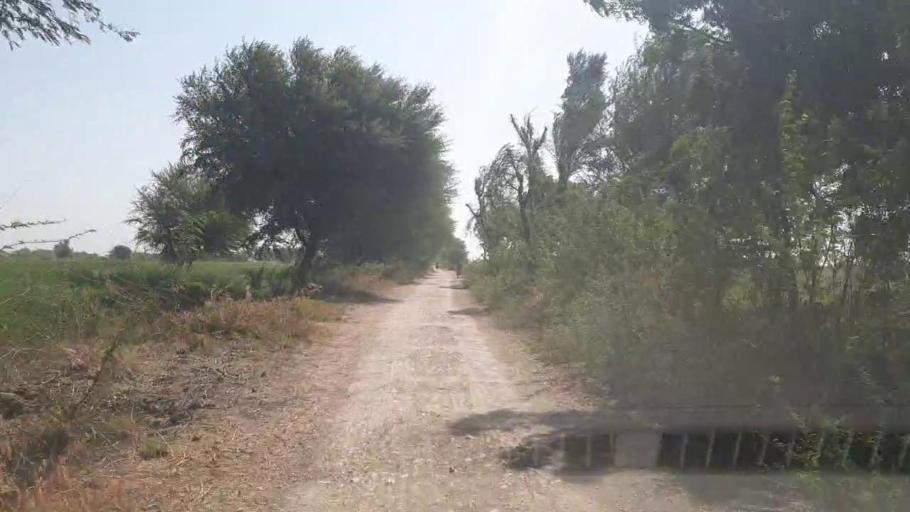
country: PK
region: Sindh
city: Kunri
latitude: 25.2714
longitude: 69.6331
